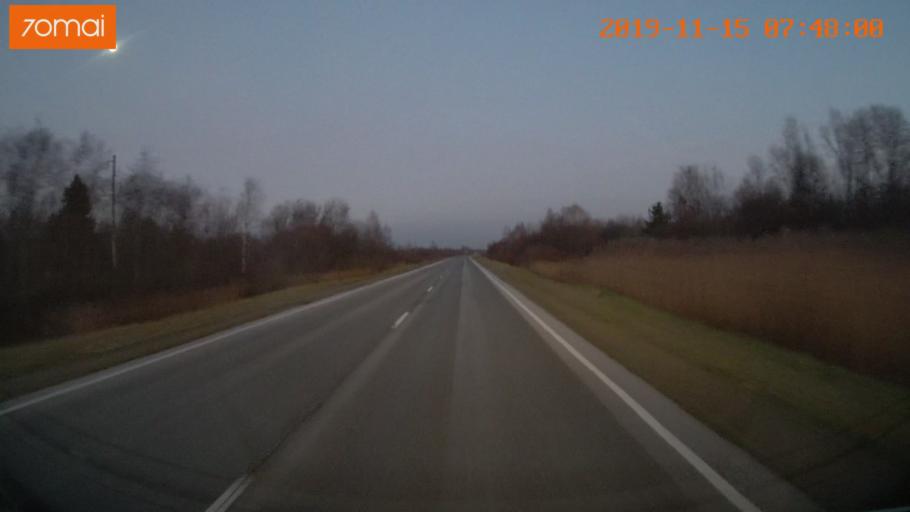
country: RU
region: Vologda
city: Sheksna
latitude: 58.8464
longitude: 38.2515
